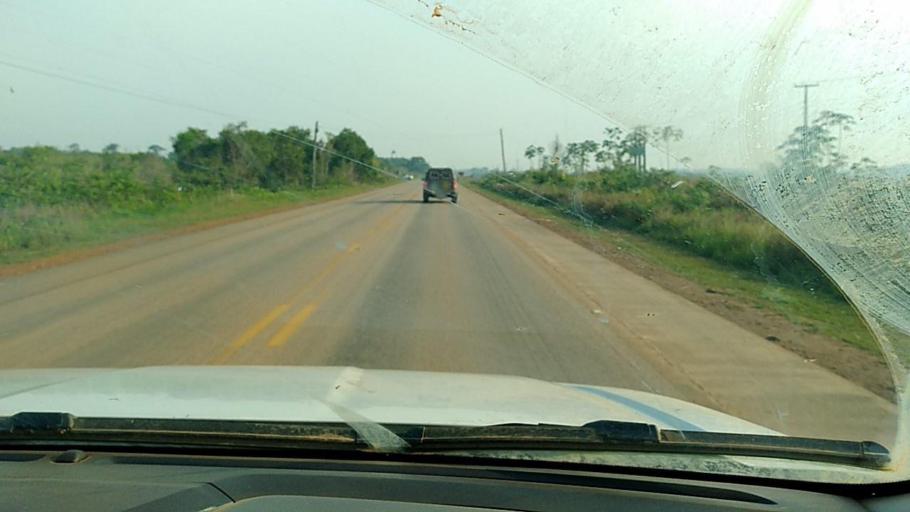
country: BR
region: Rondonia
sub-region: Porto Velho
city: Porto Velho
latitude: -8.6545
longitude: -63.9959
